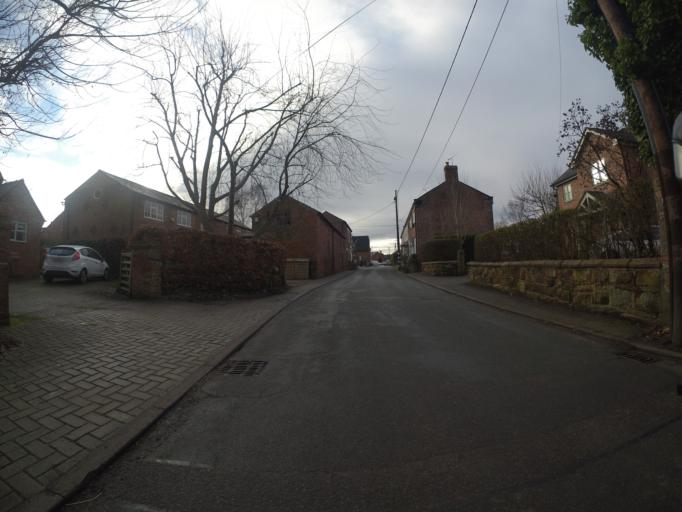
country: GB
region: England
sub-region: Cheshire West and Chester
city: Tiverton
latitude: 53.1168
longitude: -2.6504
